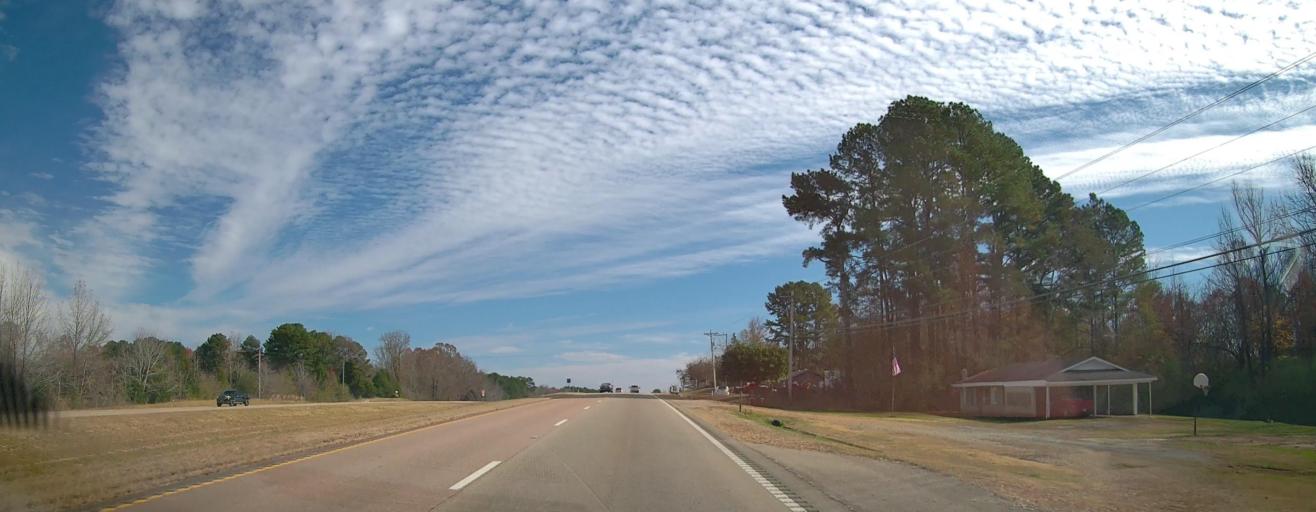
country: US
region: Mississippi
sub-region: Tippah County
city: Ripley
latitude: 34.9542
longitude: -88.8429
